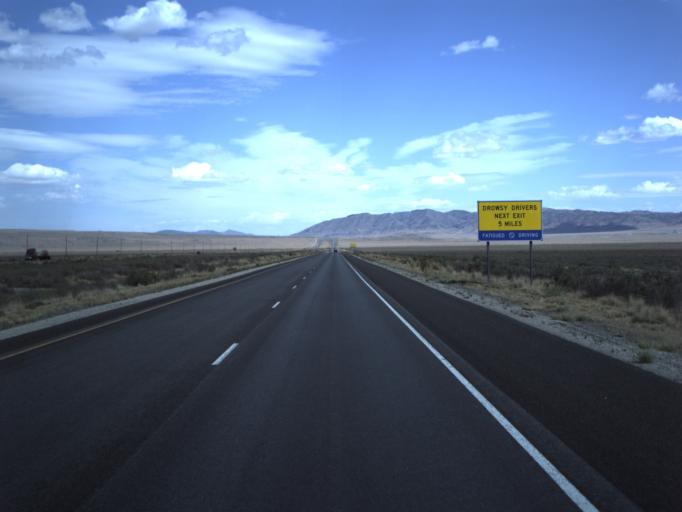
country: US
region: Utah
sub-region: Tooele County
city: Grantsville
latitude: 40.7354
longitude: -113.0994
